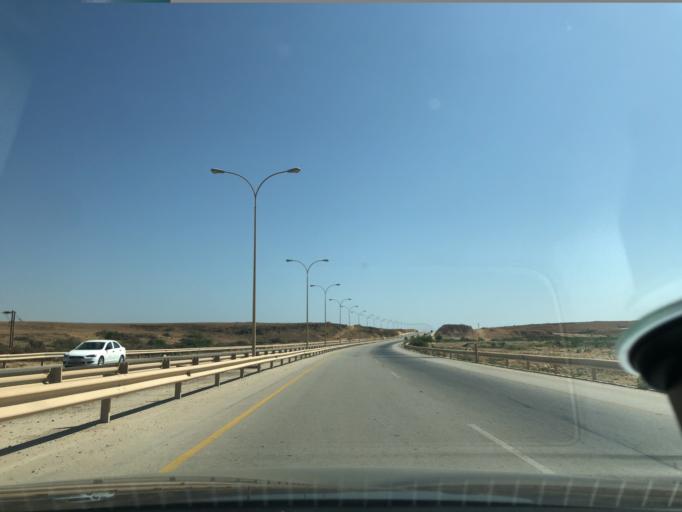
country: OM
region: Zufar
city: Salalah
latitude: 17.0491
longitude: 54.3302
